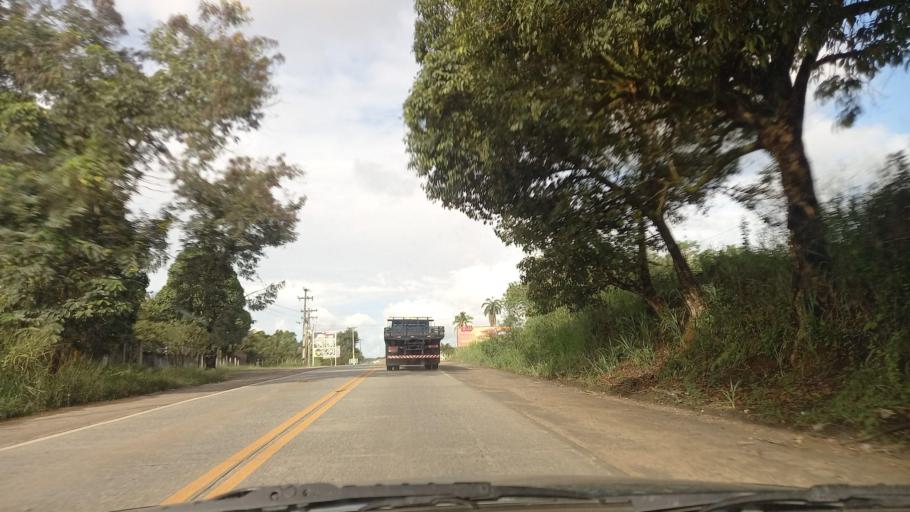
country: BR
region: Pernambuco
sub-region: Palmares
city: Palmares
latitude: -8.6910
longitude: -35.6107
